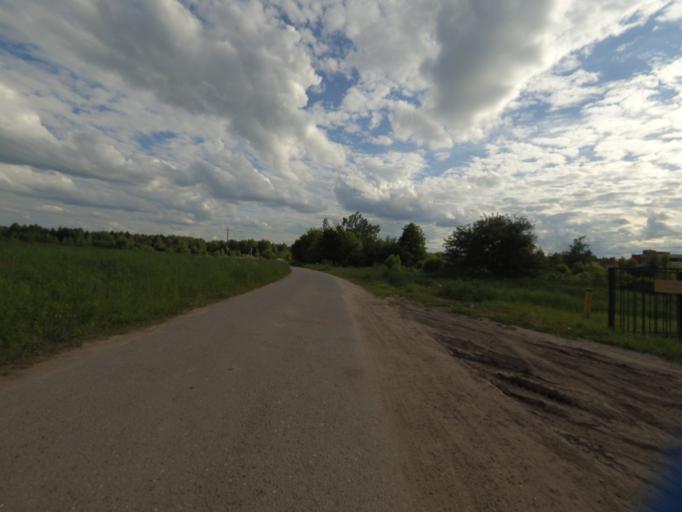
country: RU
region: Moskovskaya
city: Nekrasovskiy
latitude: 56.0838
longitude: 37.5020
